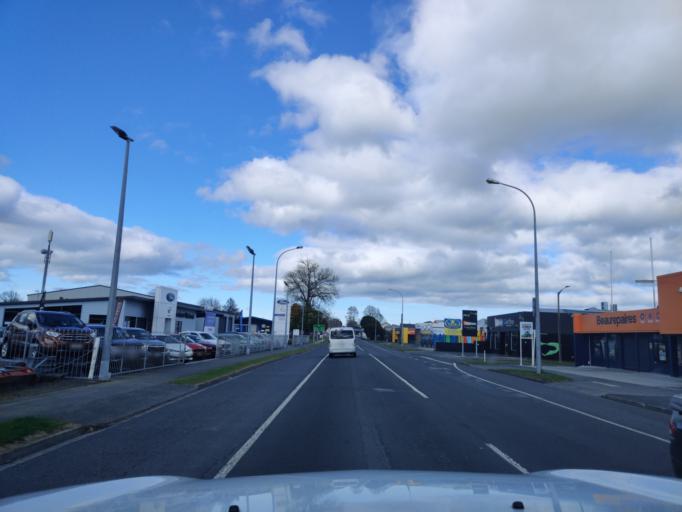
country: NZ
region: Waikato
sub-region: Matamata-Piako District
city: Matamata
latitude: -37.8112
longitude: 175.7706
